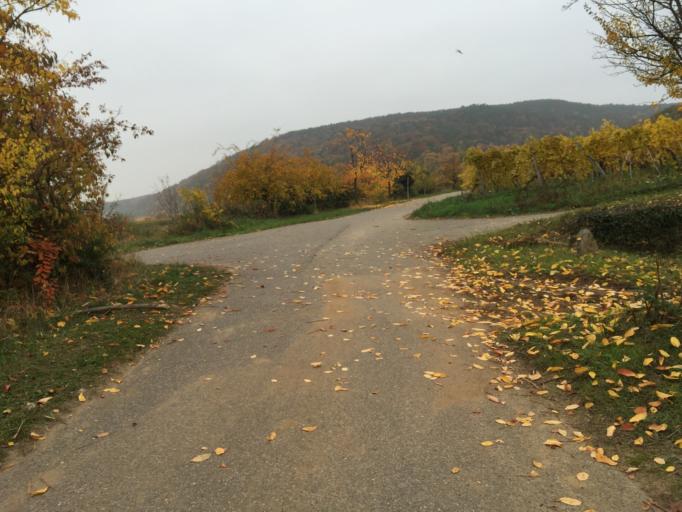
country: DE
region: Rheinland-Pfalz
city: Deidesheim
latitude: 49.4144
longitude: 8.1748
